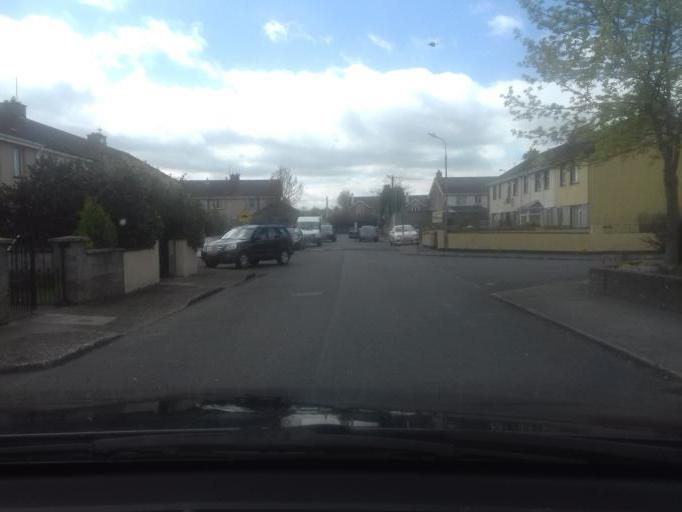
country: IE
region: Leinster
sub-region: Laois
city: Portlaoise
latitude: 53.0422
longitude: -7.3087
